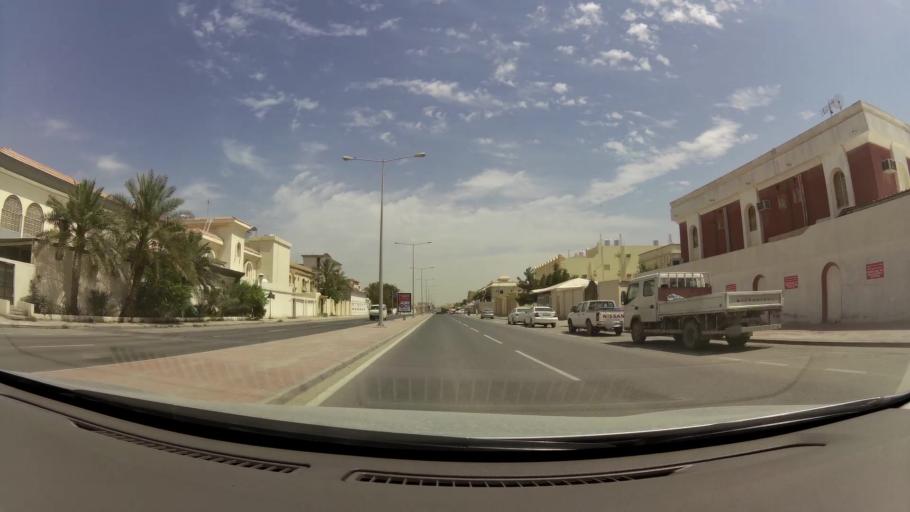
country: QA
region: Baladiyat ar Rayyan
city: Ar Rayyan
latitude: 25.2838
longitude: 51.4162
